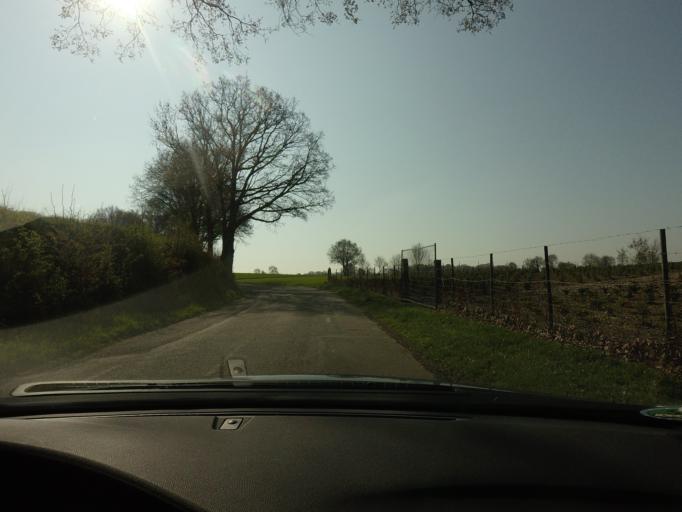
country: NL
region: Limburg
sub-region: Eijsden-Margraten
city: Margraten
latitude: 50.8272
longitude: 5.8037
